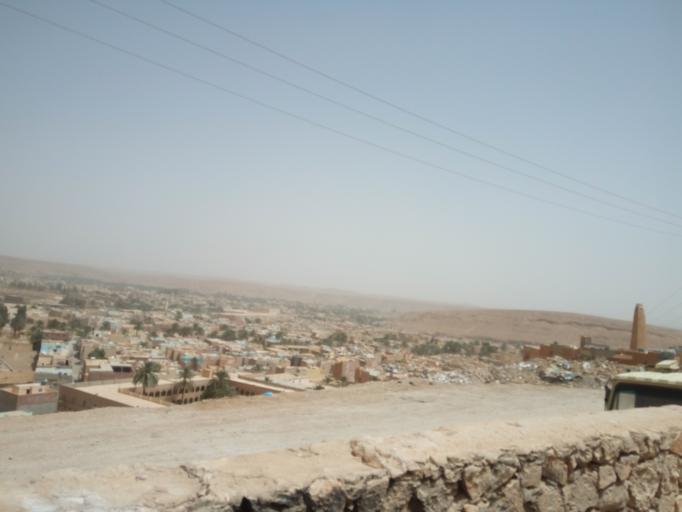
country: DZ
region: Ghardaia
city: Ghardaia
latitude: 32.4736
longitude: 3.6929
